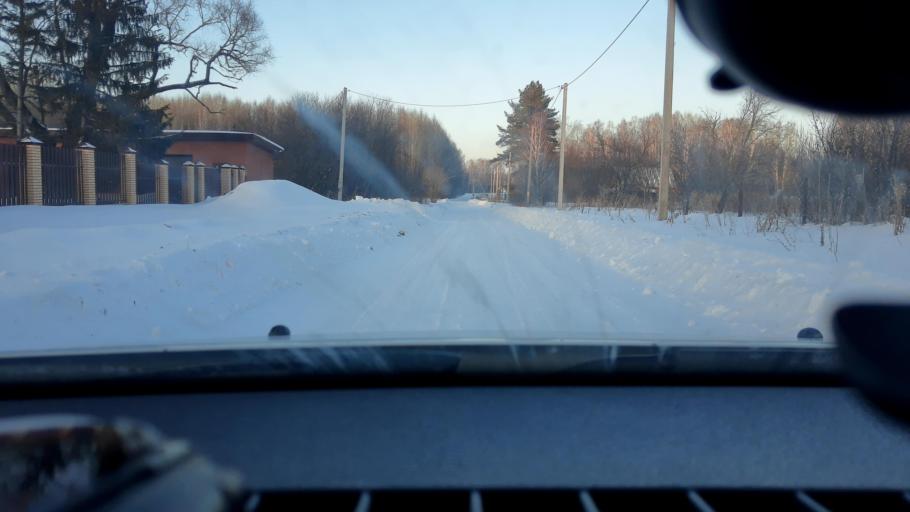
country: RU
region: Bashkortostan
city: Kudeyevskiy
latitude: 54.7985
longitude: 56.6752
